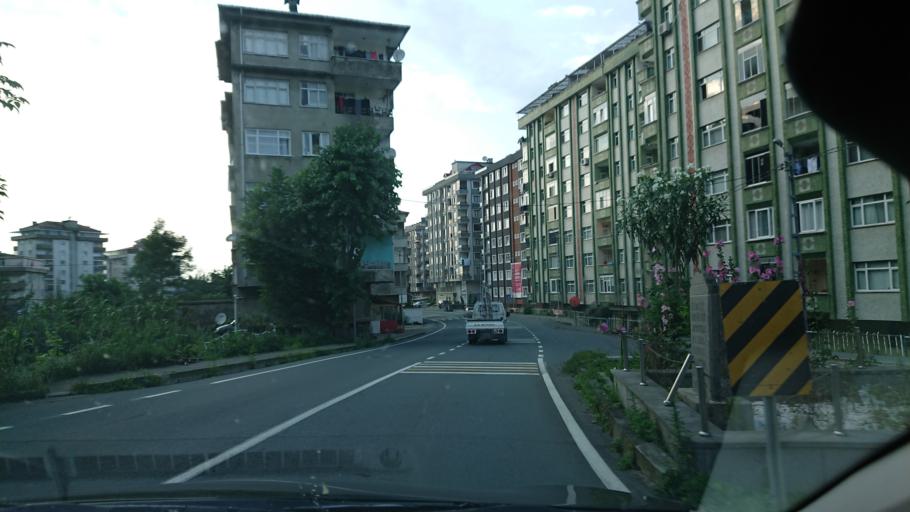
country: TR
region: Rize
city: Cayeli
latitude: 41.0803
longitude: 40.7126
